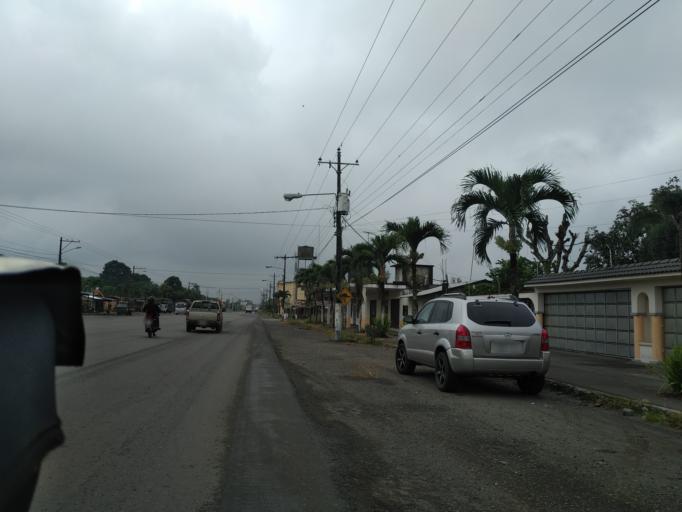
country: EC
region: Cotopaxi
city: La Mana
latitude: -0.9445
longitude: -79.3272
